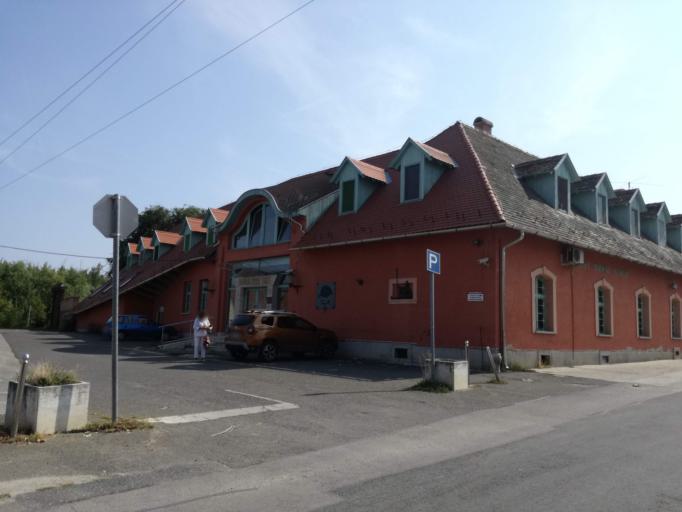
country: HU
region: Pest
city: Szazhalombatta
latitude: 47.3577
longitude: 18.9365
